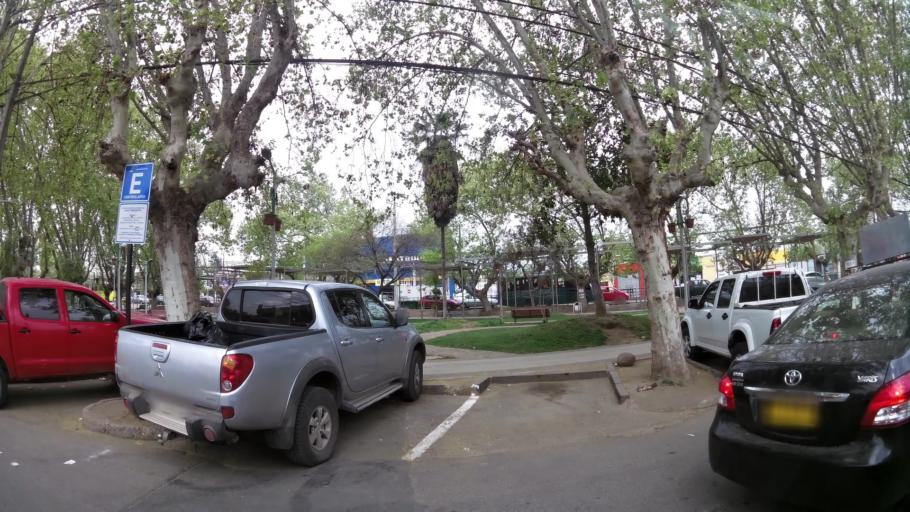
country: CL
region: Santiago Metropolitan
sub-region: Provincia de Chacabuco
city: Chicureo Abajo
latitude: -33.2029
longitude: -70.6753
